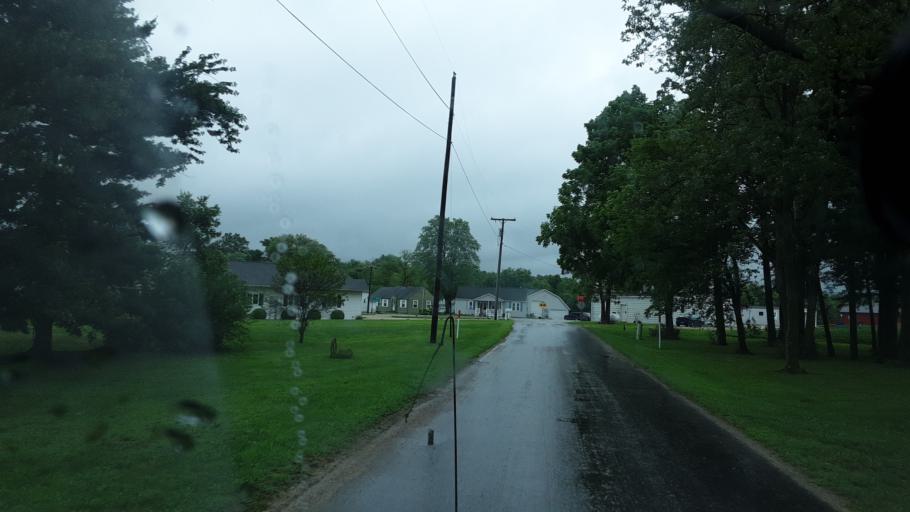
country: US
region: Indiana
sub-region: Adams County
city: Decatur
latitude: 40.7758
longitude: -84.8428
